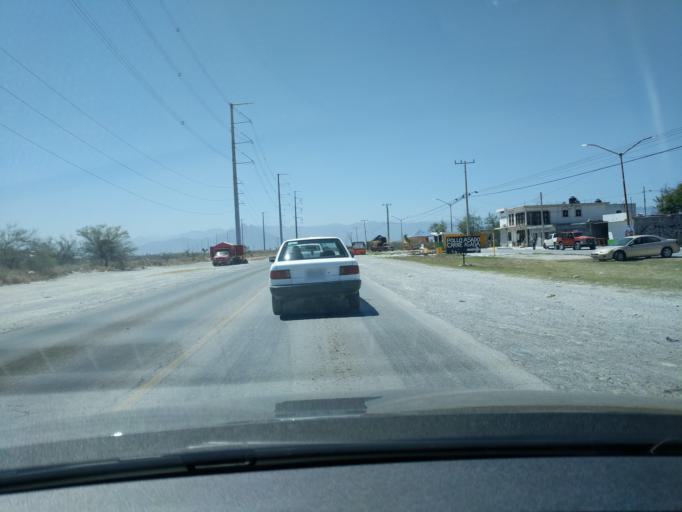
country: MX
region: Nuevo Leon
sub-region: Apodaca
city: Artemio Trevino
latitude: 25.8338
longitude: -100.1400
